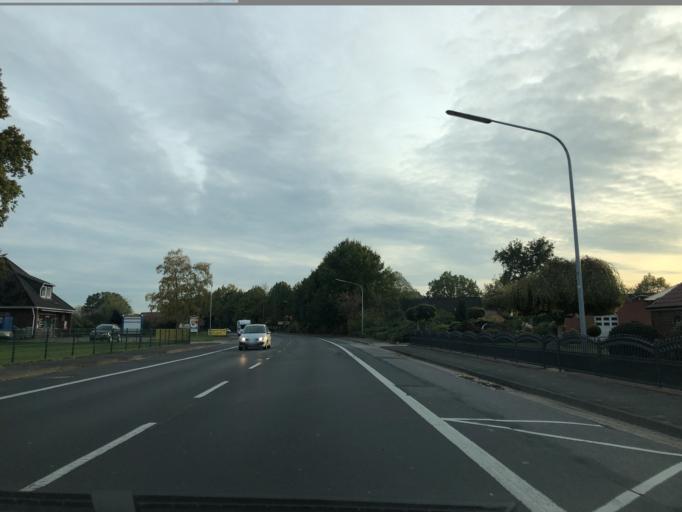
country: DE
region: Lower Saxony
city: Lehe
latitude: 53.0295
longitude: 7.3244
